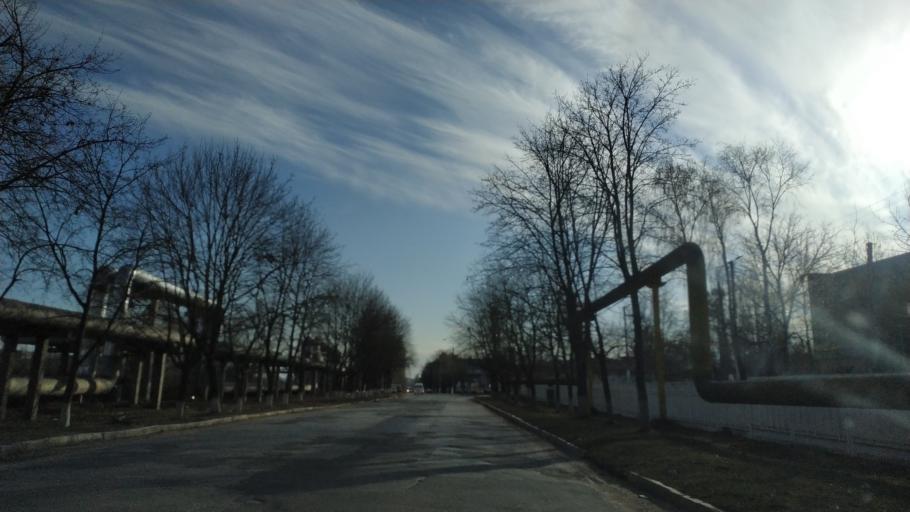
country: MD
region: Chisinau
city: Chisinau
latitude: 47.0279
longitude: 28.8960
